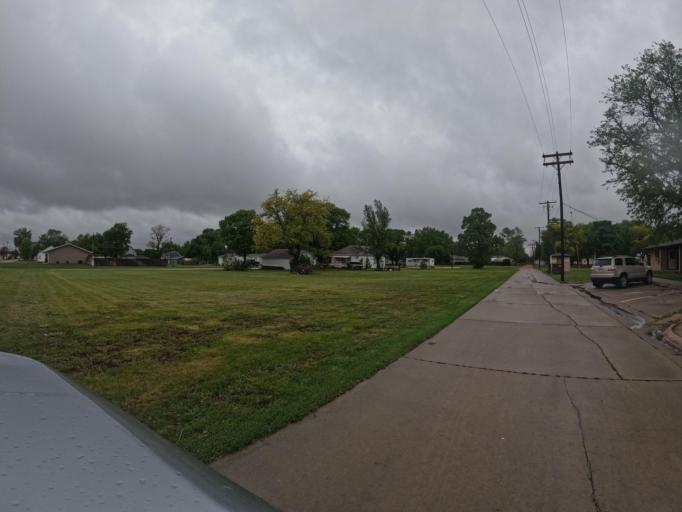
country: US
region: Nebraska
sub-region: Clay County
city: Harvard
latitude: 40.6182
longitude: -98.0924
